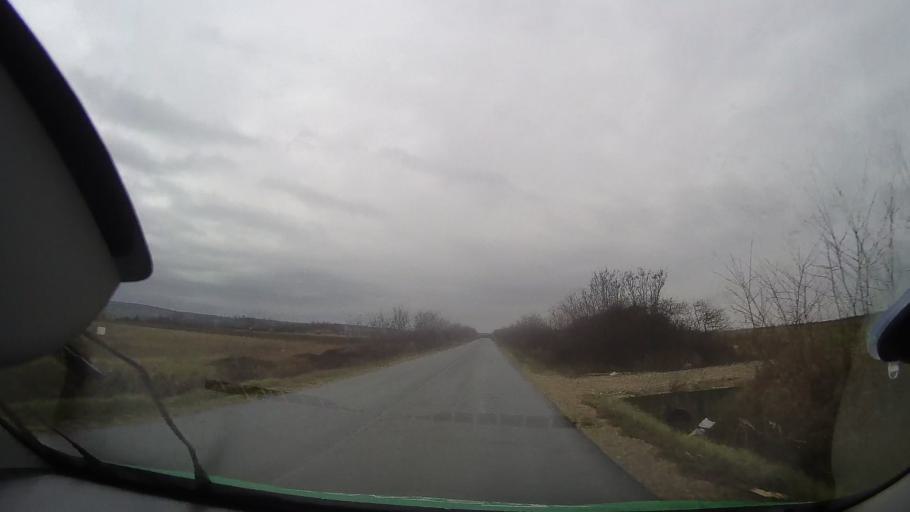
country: RO
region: Bihor
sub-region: Comuna Cociuba Mare
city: Cociuba Mare
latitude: 46.6993
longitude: 22.0337
